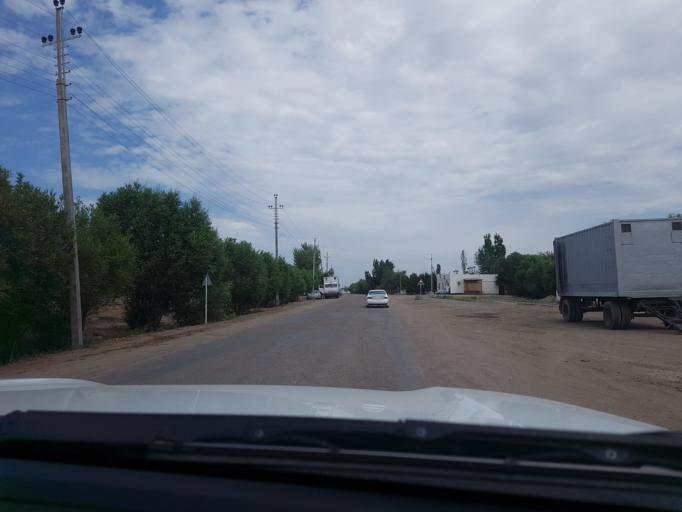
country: TM
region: Dasoguz
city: Koeneuergench
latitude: 42.3144
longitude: 59.1386
